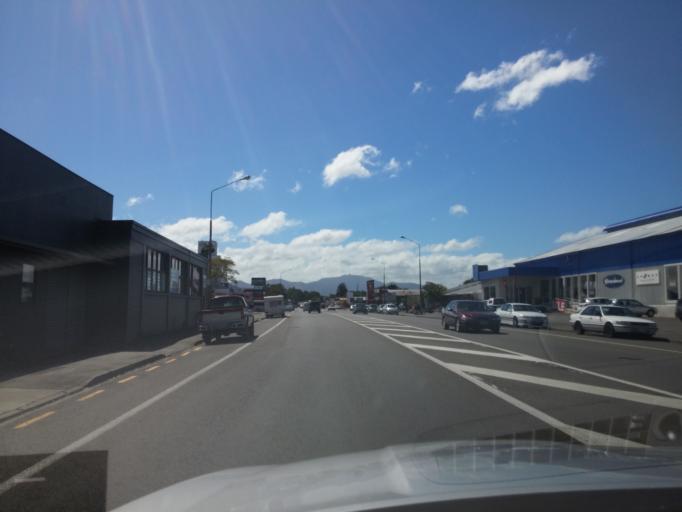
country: NZ
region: Marlborough
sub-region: Marlborough District
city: Blenheim
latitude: -41.5056
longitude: 173.9598
